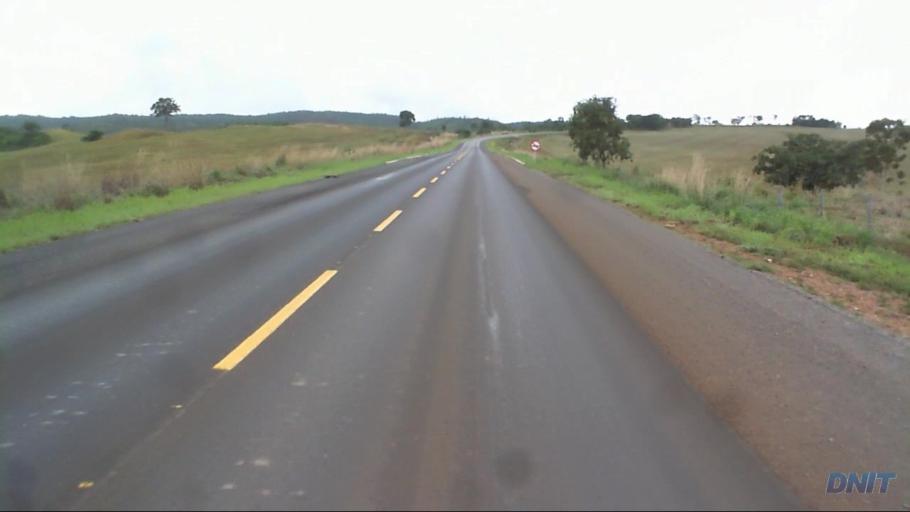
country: BR
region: Goias
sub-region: Padre Bernardo
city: Padre Bernardo
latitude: -15.2112
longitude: -48.4882
